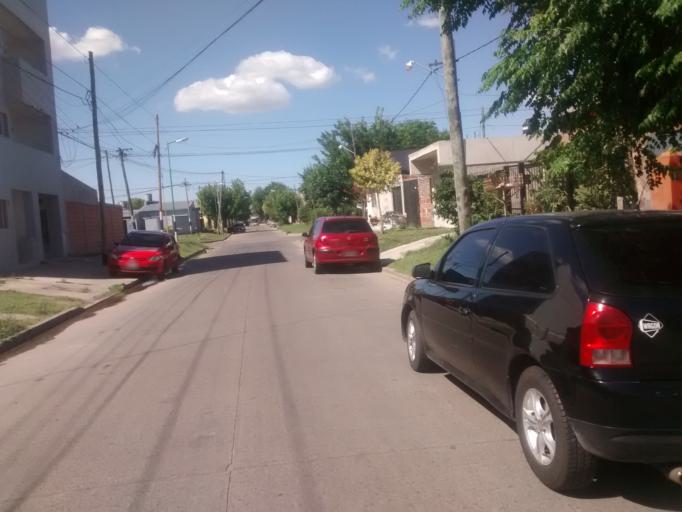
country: AR
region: Buenos Aires
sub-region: Partido de La Plata
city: La Plata
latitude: -34.9330
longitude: -57.9125
